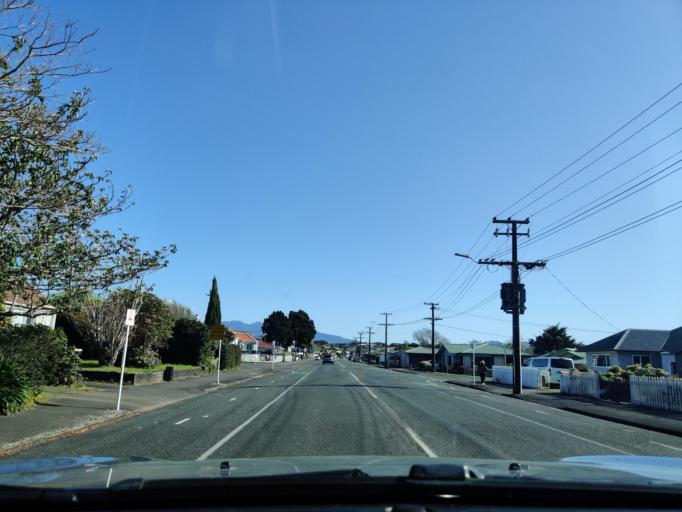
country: NZ
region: Taranaki
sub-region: New Plymouth District
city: New Plymouth
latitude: -39.0755
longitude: 174.0571
